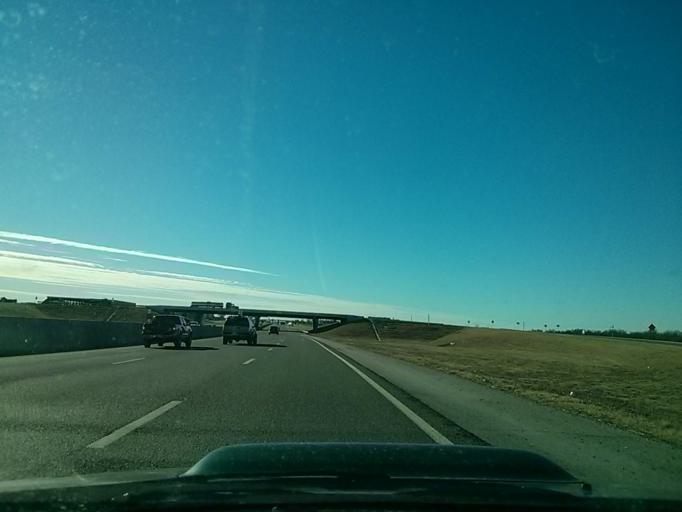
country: US
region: Oklahoma
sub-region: Tulsa County
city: Owasso
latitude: 36.2231
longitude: -95.8519
